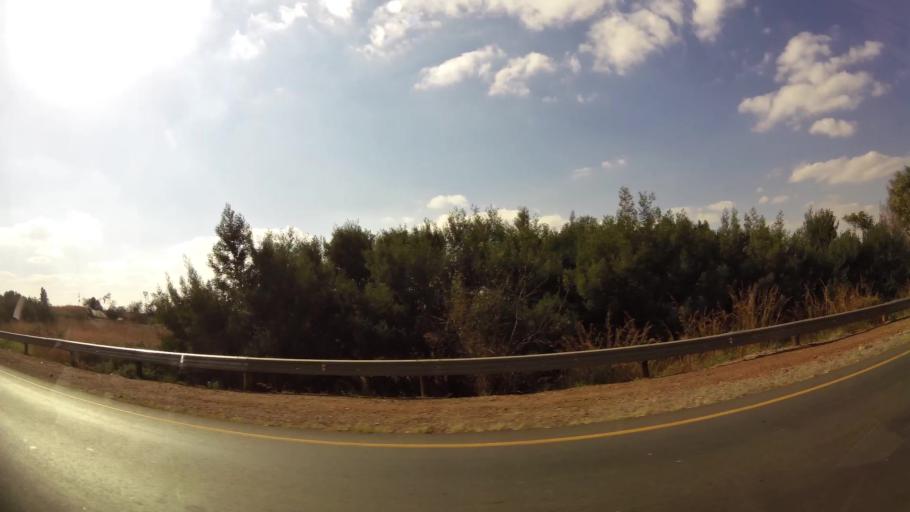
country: ZA
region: Gauteng
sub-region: West Rand District Municipality
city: Krugersdorp
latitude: -26.0398
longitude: 27.7737
